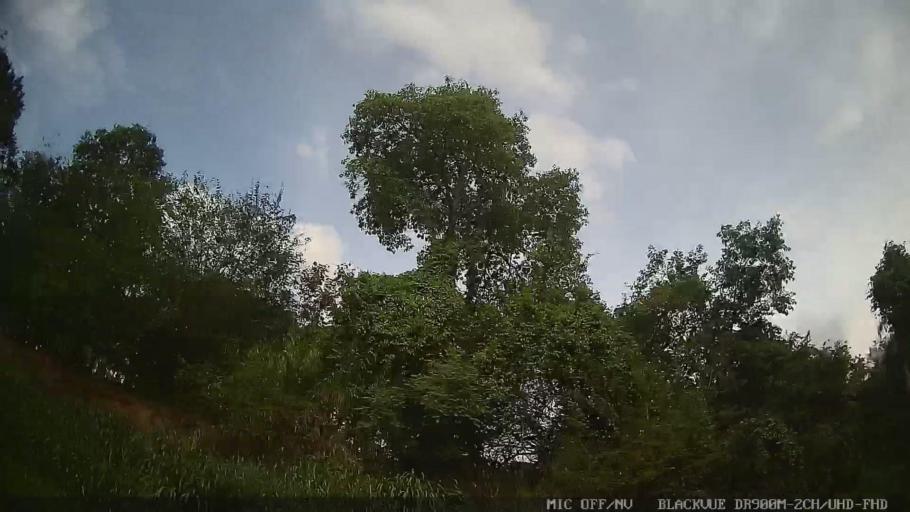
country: BR
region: Sao Paulo
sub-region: Amparo
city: Amparo
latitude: -22.7401
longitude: -46.7578
